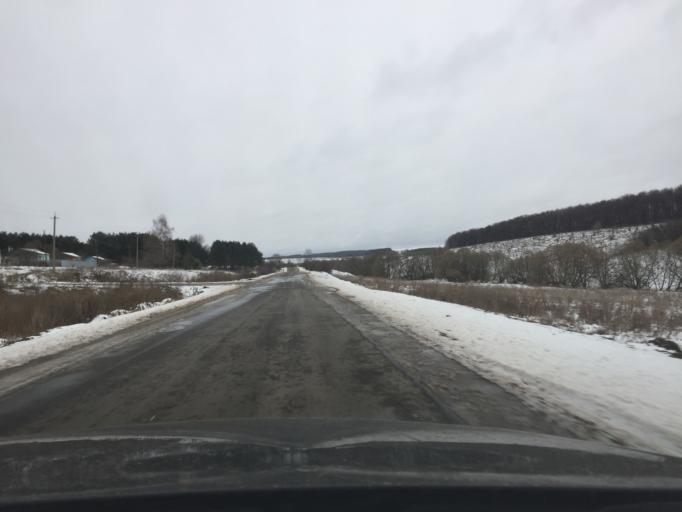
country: RU
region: Tula
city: Shchekino
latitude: 53.8266
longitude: 37.5590
